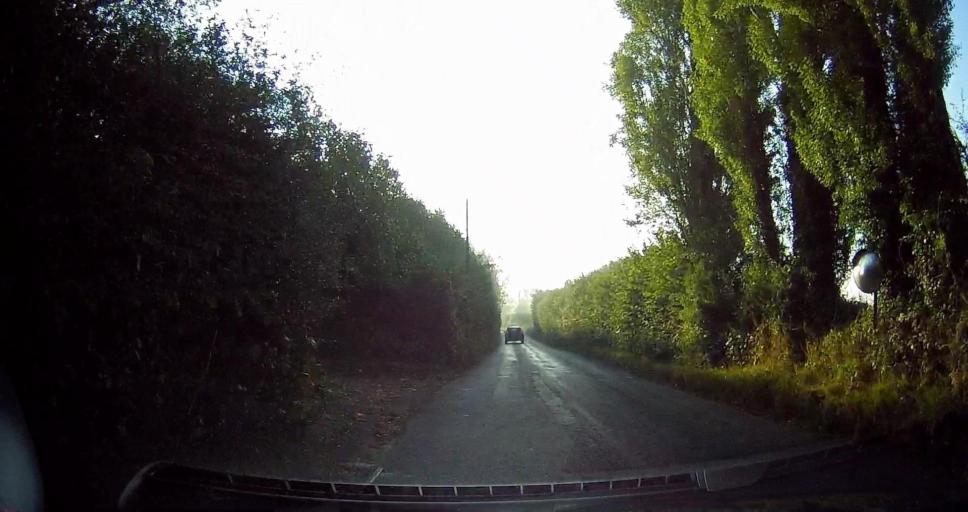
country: GB
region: England
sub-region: Kent
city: Kennington
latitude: 51.1860
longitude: 0.9017
